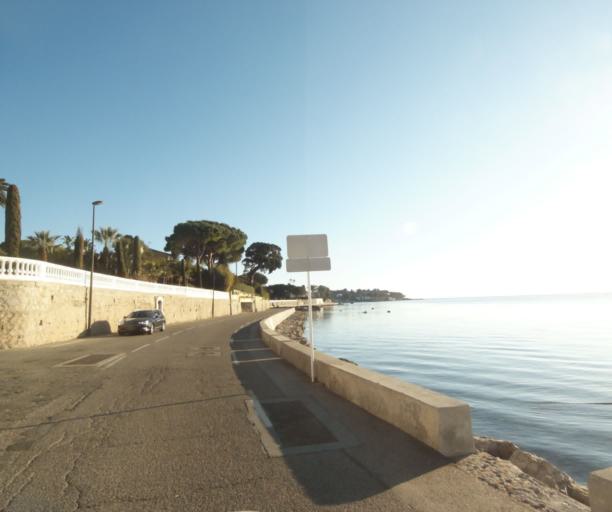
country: FR
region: Provence-Alpes-Cote d'Azur
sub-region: Departement des Alpes-Maritimes
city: Antibes
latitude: 43.5595
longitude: 7.1217
